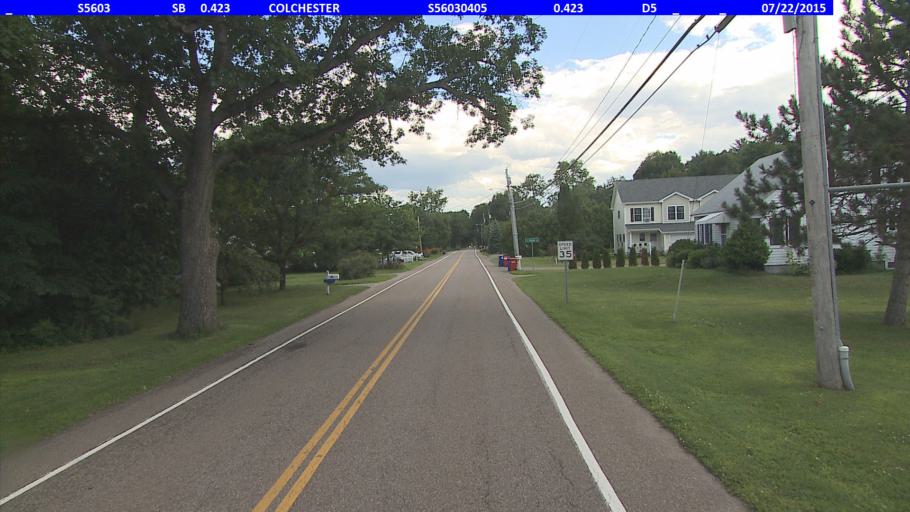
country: US
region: Vermont
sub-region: Chittenden County
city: Burlington
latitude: 44.5441
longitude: -73.2502
